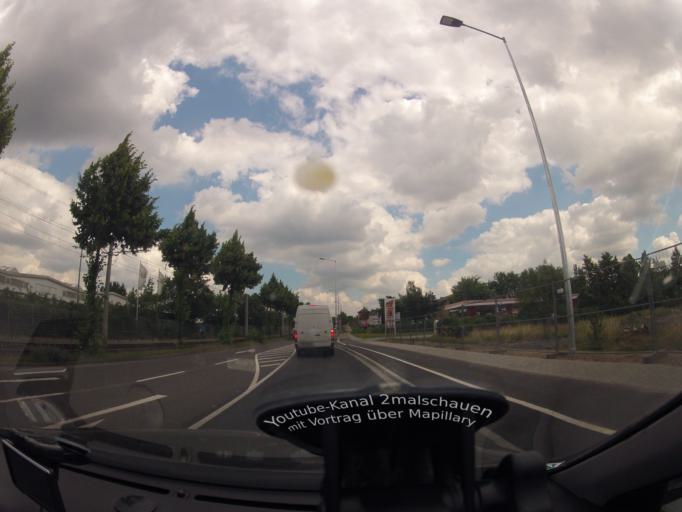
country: DE
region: Saxony
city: Taucha
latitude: 51.3568
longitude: 12.4367
